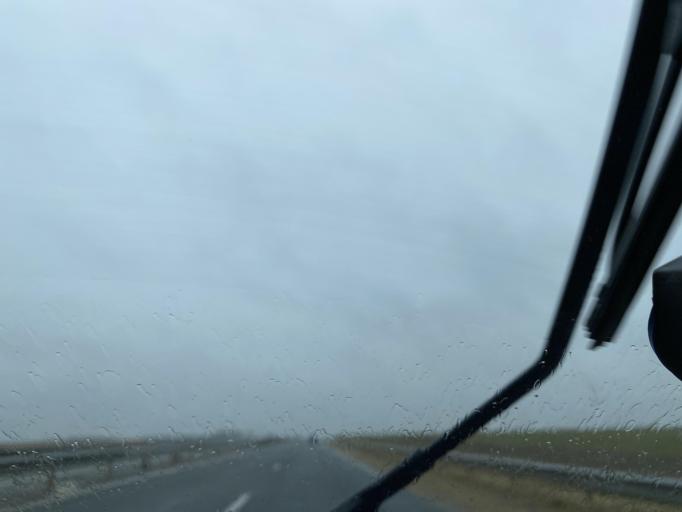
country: FR
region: Centre
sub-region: Departement d'Eure-et-Loir
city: Bailleau-l'Eveque
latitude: 48.5812
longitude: 1.4300
